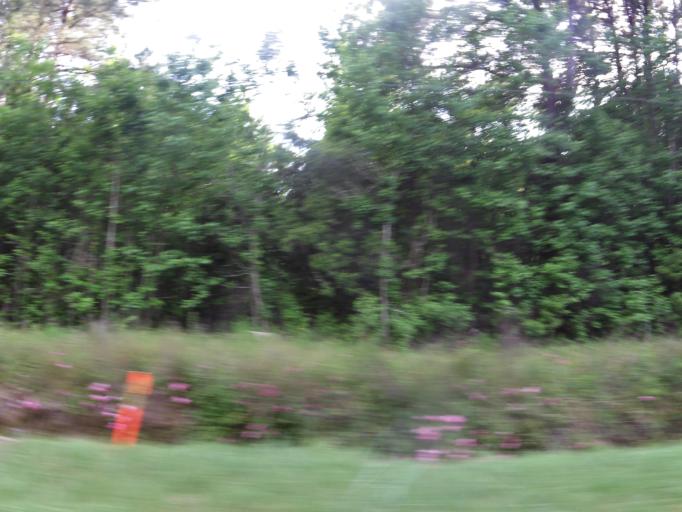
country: US
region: South Carolina
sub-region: Jasper County
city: Ridgeland
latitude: 32.5270
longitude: -81.1514
